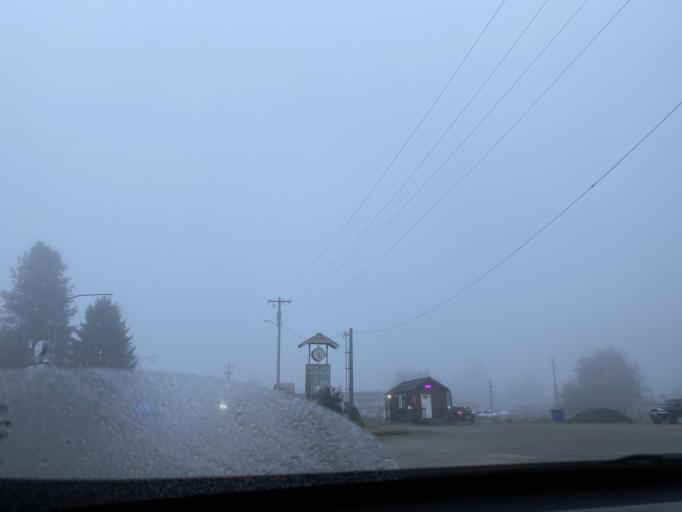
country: US
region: Washington
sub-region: Clallam County
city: Forks
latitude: 47.9489
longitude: -124.3855
